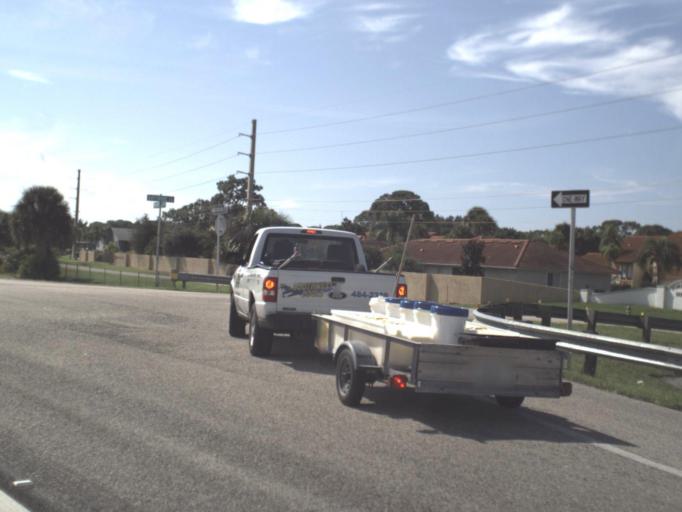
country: US
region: Florida
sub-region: Sarasota County
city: Laurel
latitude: 27.1524
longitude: -82.4672
